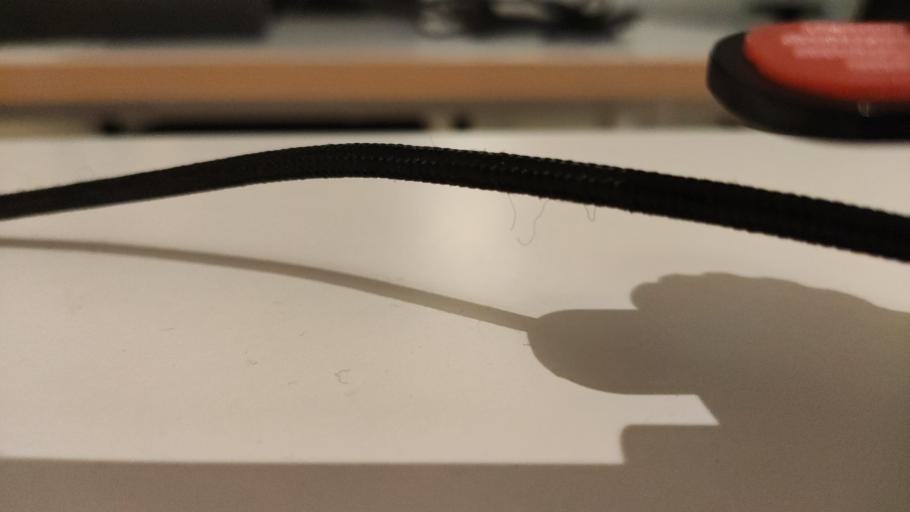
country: RU
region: Moskovskaya
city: Novoye
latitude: 55.6330
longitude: 38.9368
